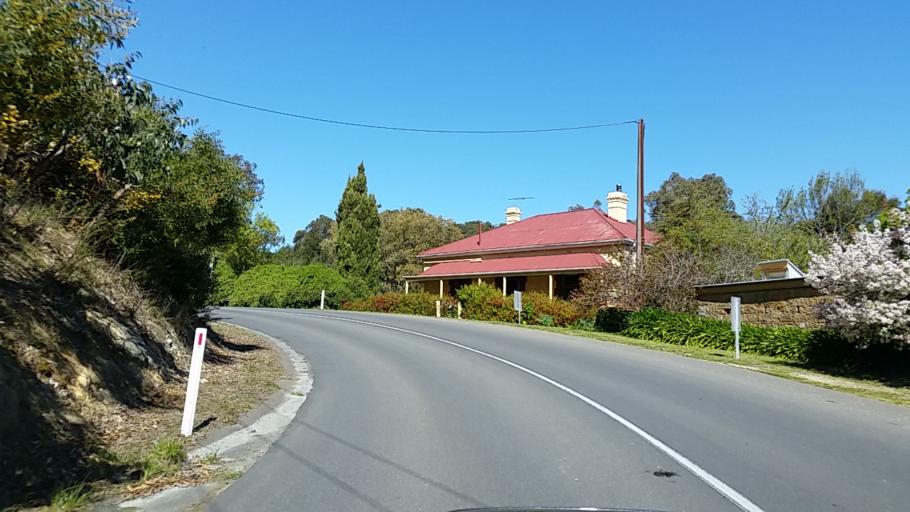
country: AU
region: South Australia
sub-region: Adelaide Hills
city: Bridgewater
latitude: -34.9571
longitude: 138.7461
